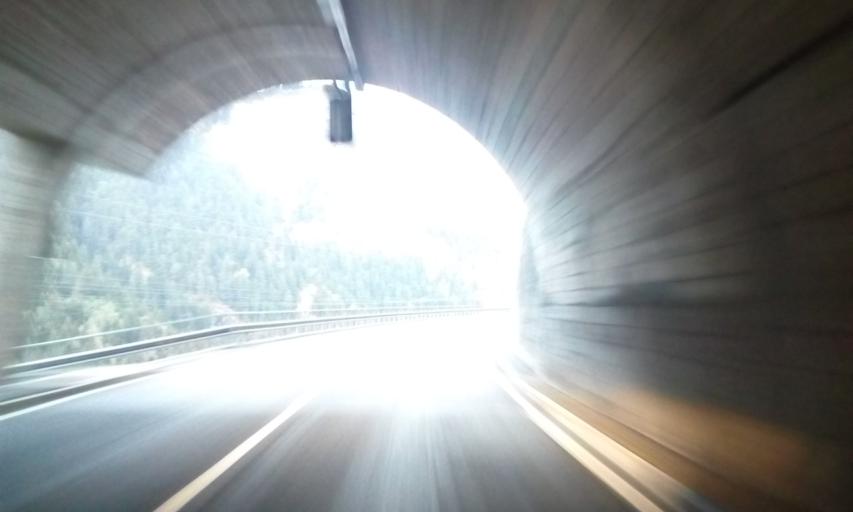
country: CH
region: Grisons
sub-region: Hinterrhein District
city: Thusis
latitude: 46.6873
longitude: 9.5040
